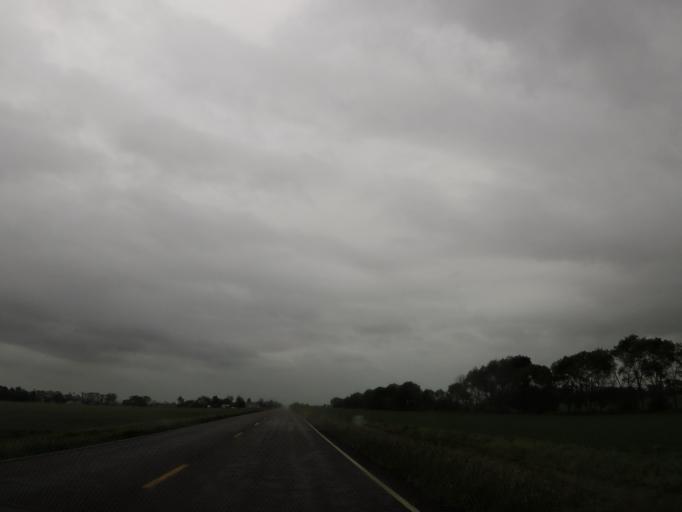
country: US
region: North Dakota
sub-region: Walsh County
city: Grafton
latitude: 48.4700
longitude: -97.3083
